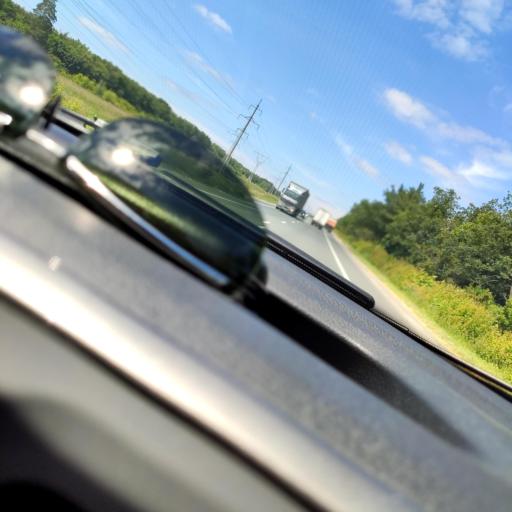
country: RU
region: Samara
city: Bogatyr'
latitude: 53.5008
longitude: 49.9511
